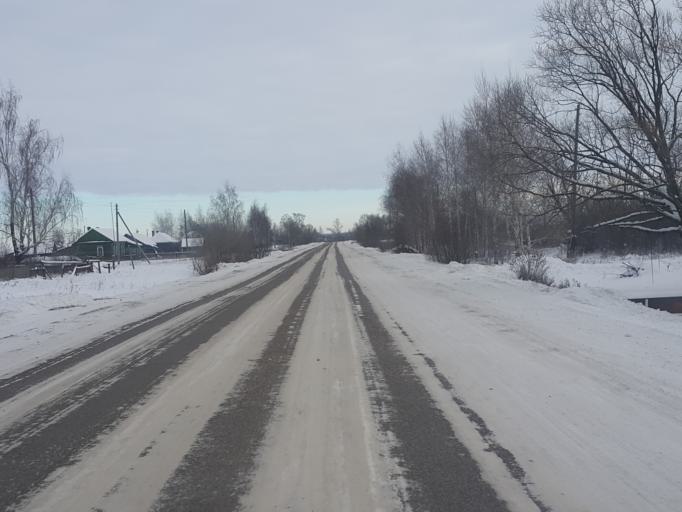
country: RU
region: Tambov
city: Platonovka
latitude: 52.8533
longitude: 41.8177
